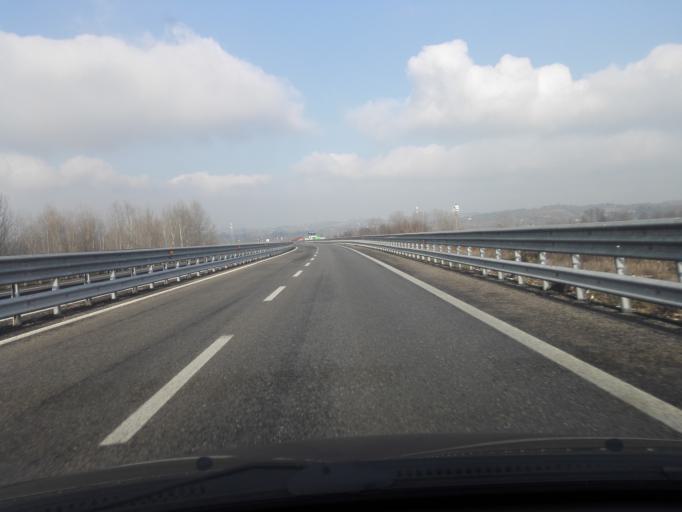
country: IT
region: Piedmont
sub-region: Provincia di Alessandria
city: Valle San Bartolomeo
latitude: 44.9278
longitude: 8.6379
